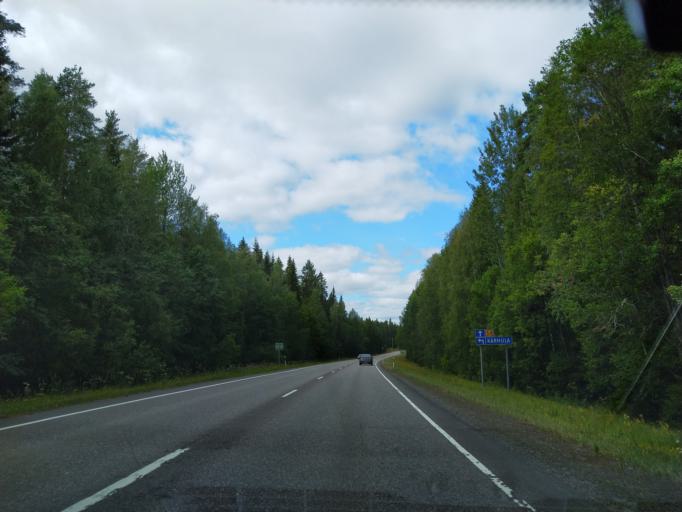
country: FI
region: Haeme
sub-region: Riihimaeki
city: Loppi
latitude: 60.7492
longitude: 24.3206
